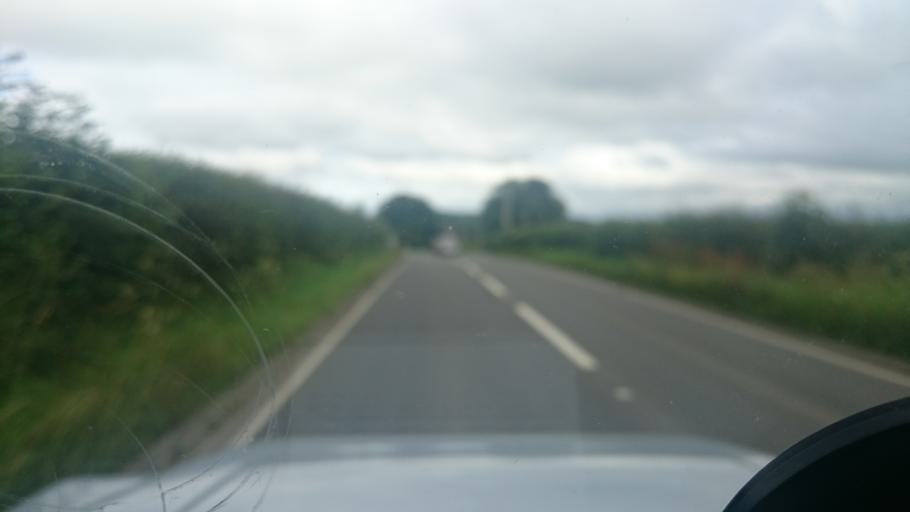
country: GB
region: Wales
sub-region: Pembrokeshire
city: Narberth
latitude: 51.8167
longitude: -4.7312
